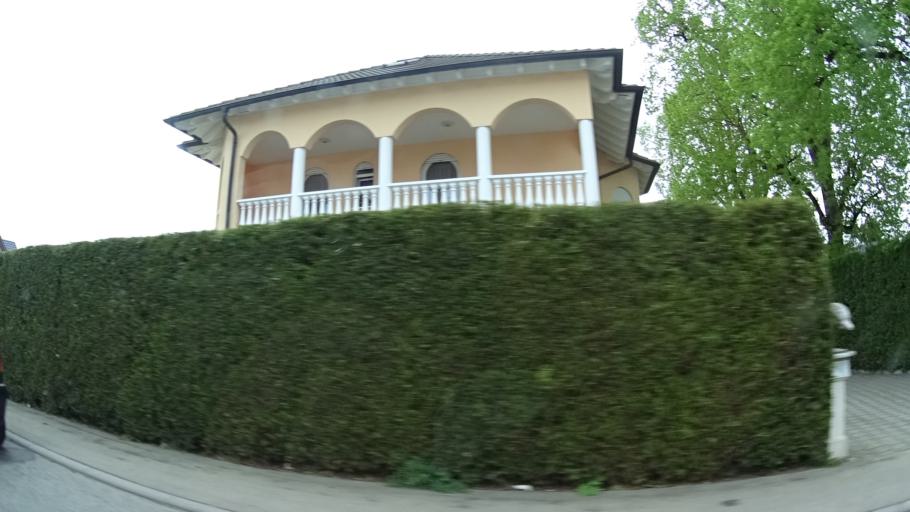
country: DE
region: Baden-Wuerttemberg
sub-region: Freiburg Region
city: Zimmern ob Rottweil
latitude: 48.1671
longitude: 8.5903
